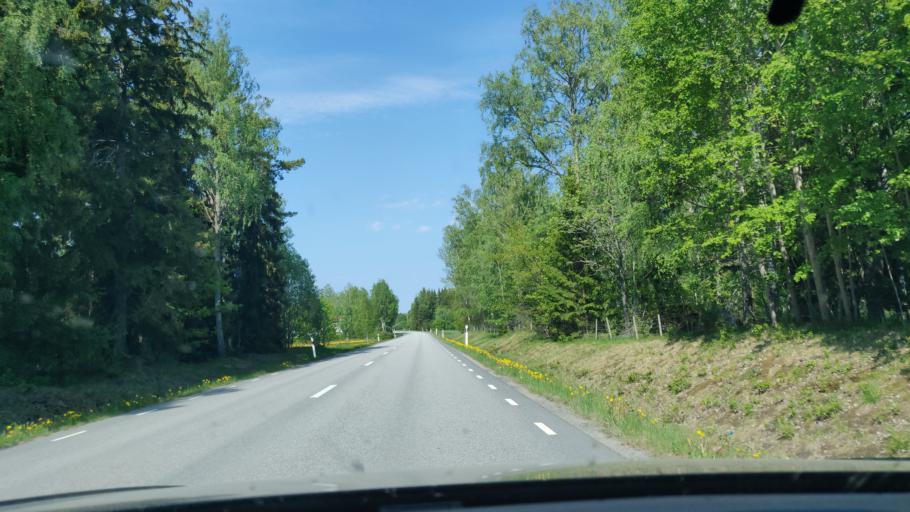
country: SE
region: Uppsala
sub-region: Heby Kommun
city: OEstervala
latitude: 60.1530
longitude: 17.2021
